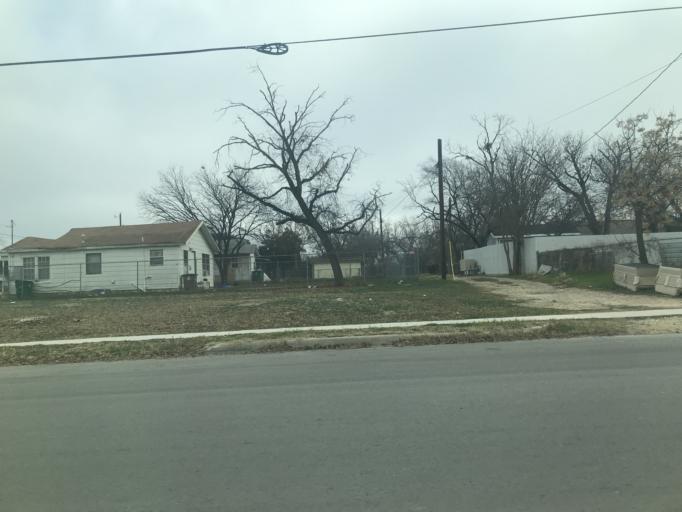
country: US
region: Texas
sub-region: Tom Green County
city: San Angelo
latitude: 31.4692
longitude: -100.4461
